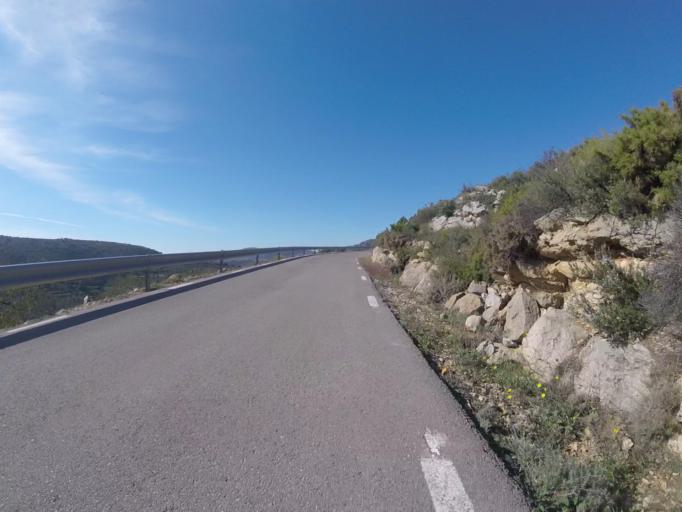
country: ES
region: Valencia
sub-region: Provincia de Castello
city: Sarratella
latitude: 40.2963
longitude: 0.0277
